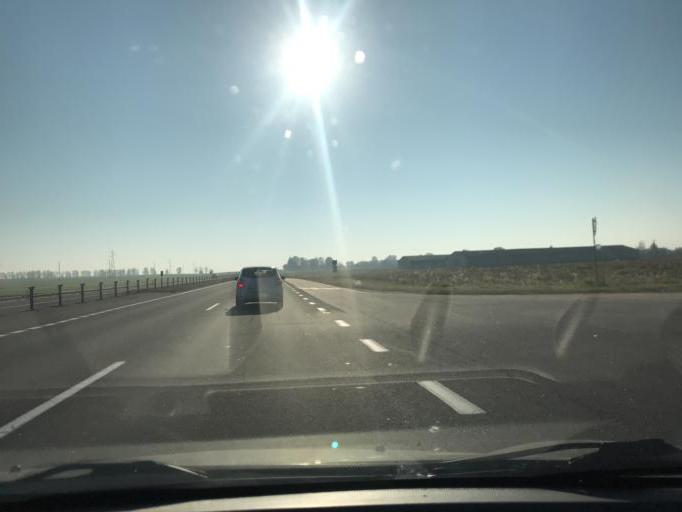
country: BY
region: Minsk
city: Mar''ina Horka
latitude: 53.5935
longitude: 28.0968
